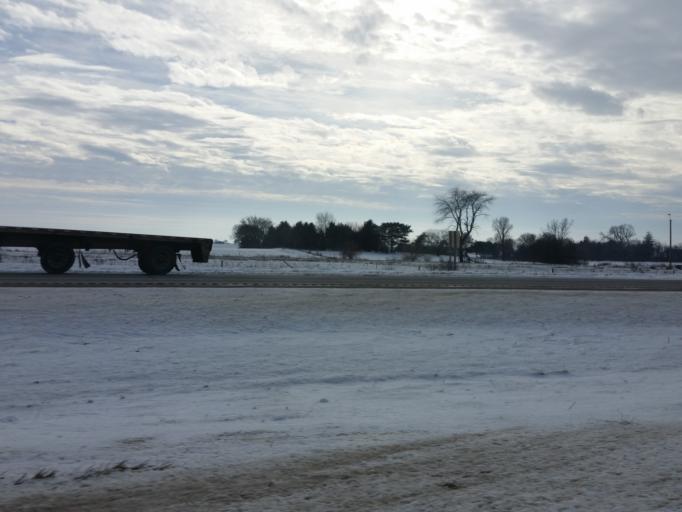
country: US
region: Iowa
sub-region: Buchanan County
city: Independence
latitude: 42.4480
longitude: -91.9236
